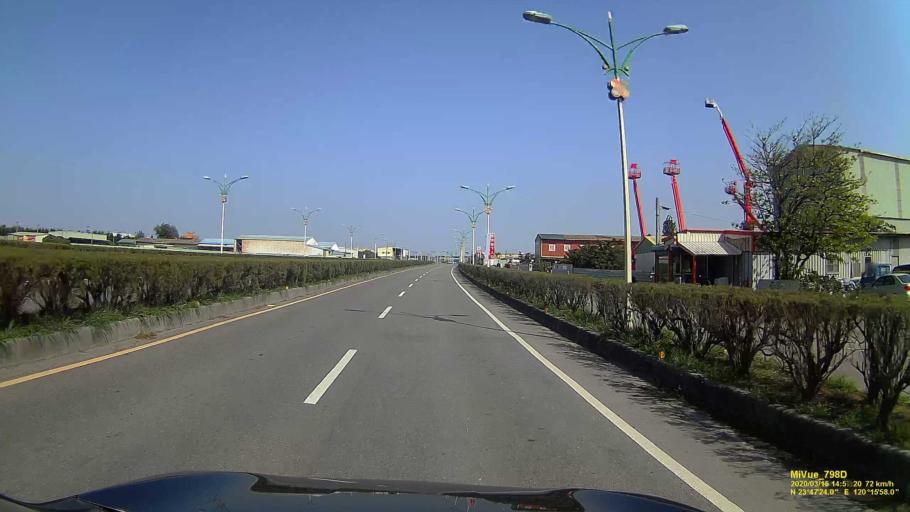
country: TW
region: Taiwan
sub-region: Yunlin
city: Douliu
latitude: 23.7899
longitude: 120.2666
